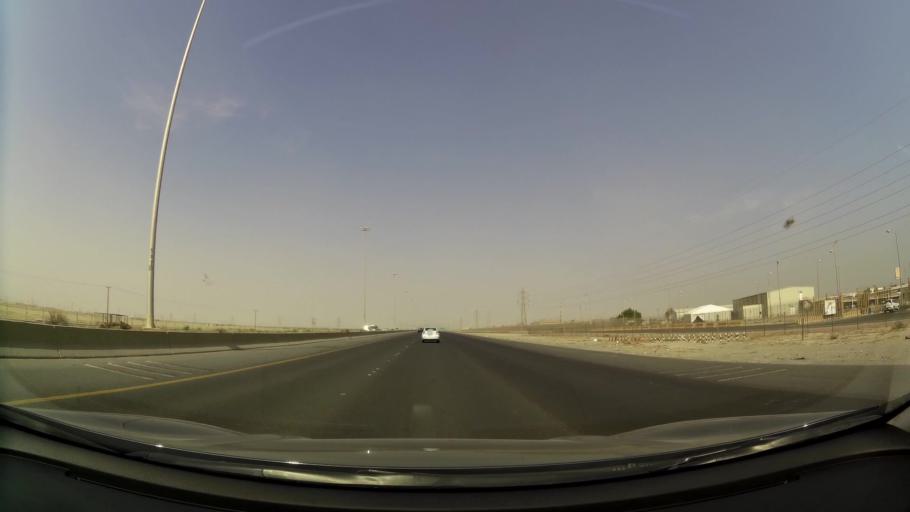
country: KW
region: Al Ahmadi
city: Al Fahahil
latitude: 29.0247
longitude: 48.1252
